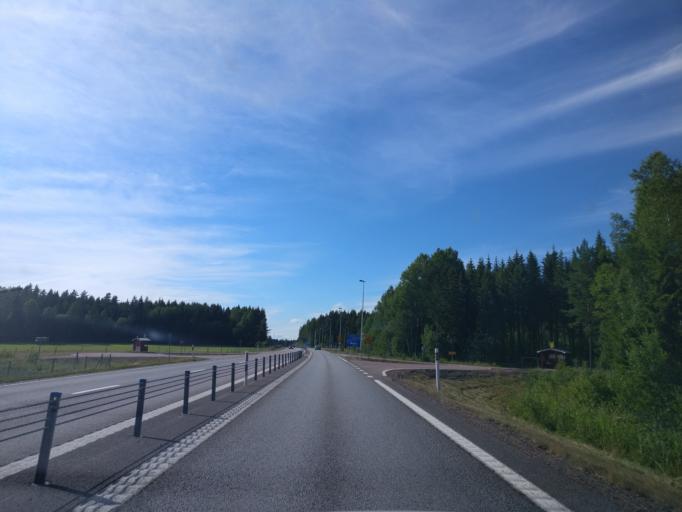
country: SE
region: Vaermland
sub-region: Kils Kommun
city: Kil
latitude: 59.4859
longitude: 13.3464
